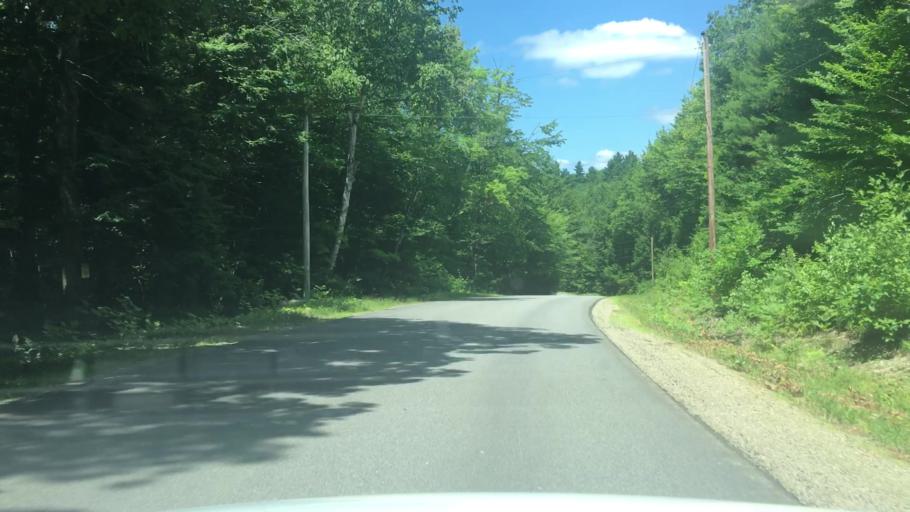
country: US
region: Maine
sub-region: Waldo County
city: Searsmont
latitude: 44.4492
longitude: -69.3077
